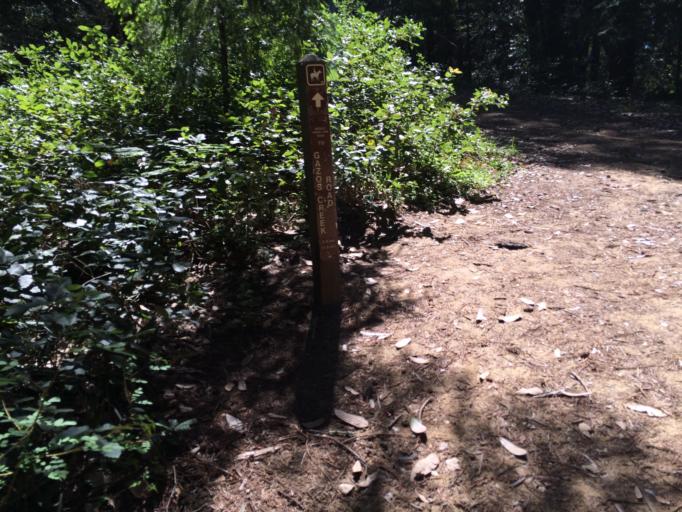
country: US
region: California
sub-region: Santa Cruz County
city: Boulder Creek
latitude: 37.1972
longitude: -122.2321
